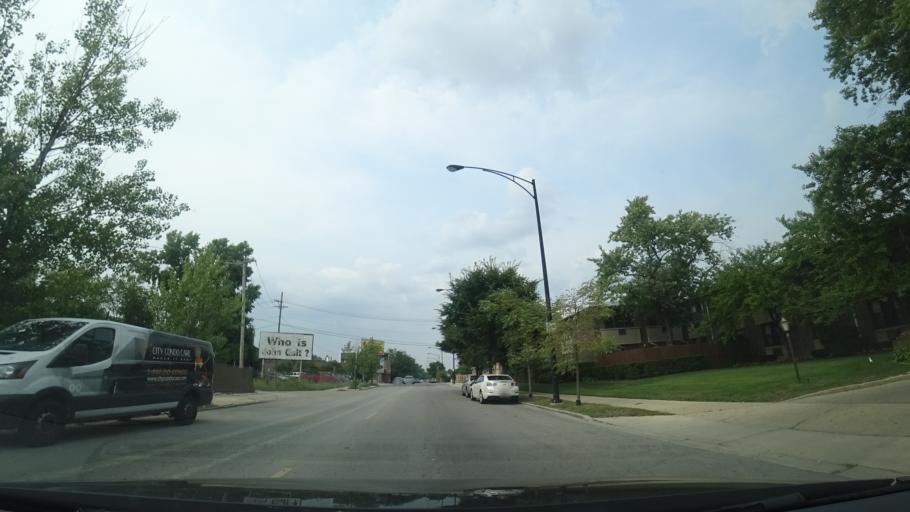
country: US
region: Illinois
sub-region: Cook County
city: Lincolnwood
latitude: 41.9931
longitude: -87.7289
